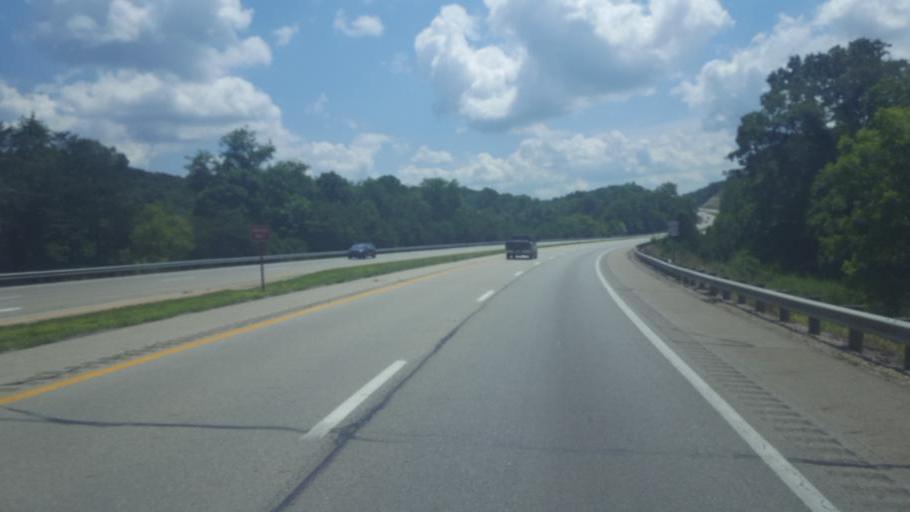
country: US
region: Ohio
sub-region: Jackson County
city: Jackson
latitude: 39.1156
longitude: -82.6828
